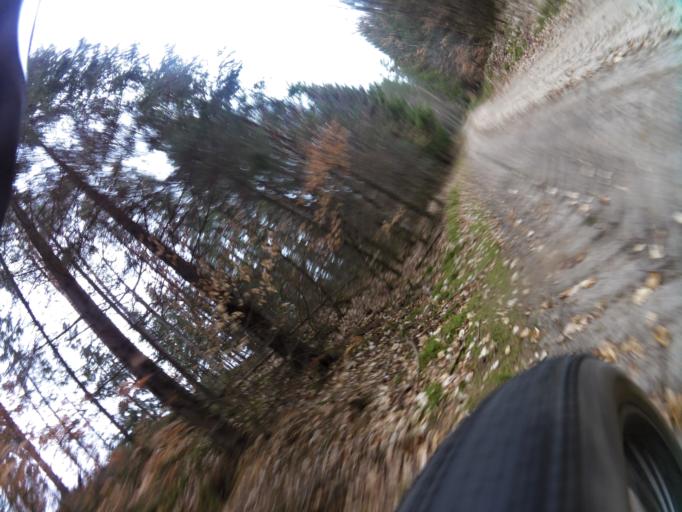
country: PL
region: West Pomeranian Voivodeship
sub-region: Powiat koszalinski
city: Polanow
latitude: 54.1707
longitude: 16.6475
